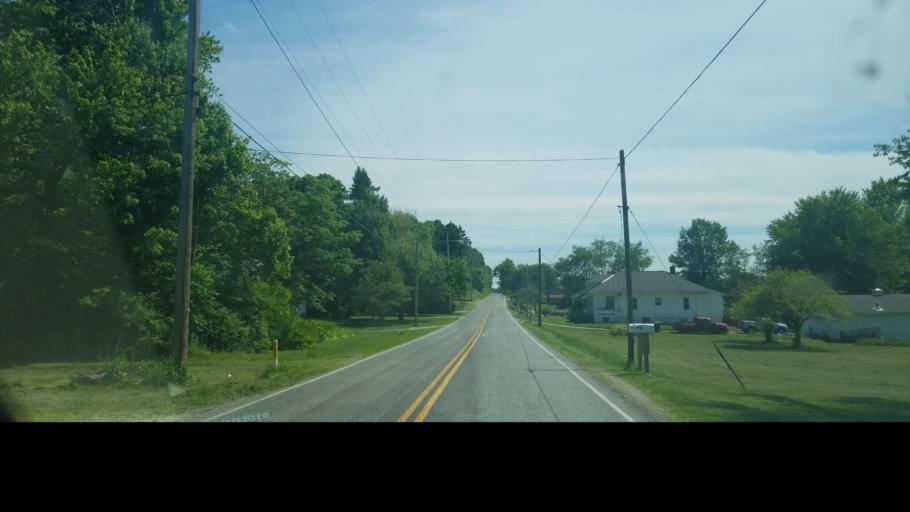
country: US
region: Ohio
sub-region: Stark County
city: Brewster
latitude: 40.7005
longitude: -81.5790
